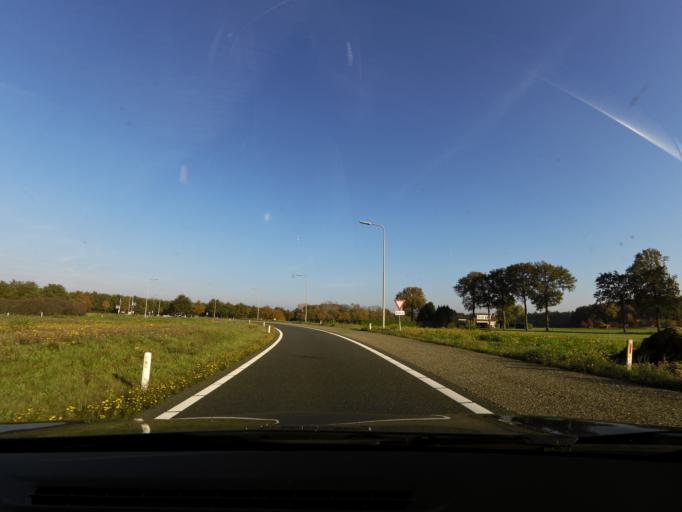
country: NL
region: North Brabant
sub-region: Gemeente Breda
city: Breda
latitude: 51.5353
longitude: 4.7984
